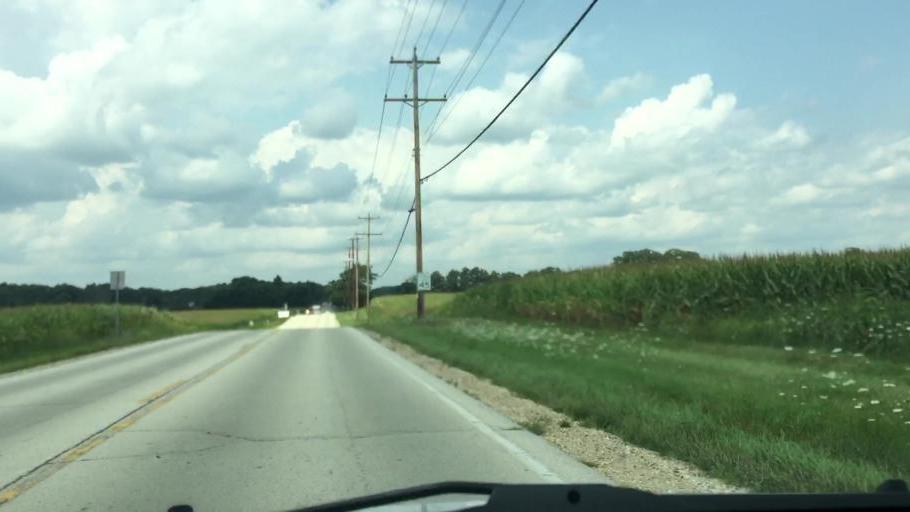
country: US
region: Wisconsin
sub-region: Waukesha County
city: North Prairie
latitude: 42.9398
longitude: -88.4055
